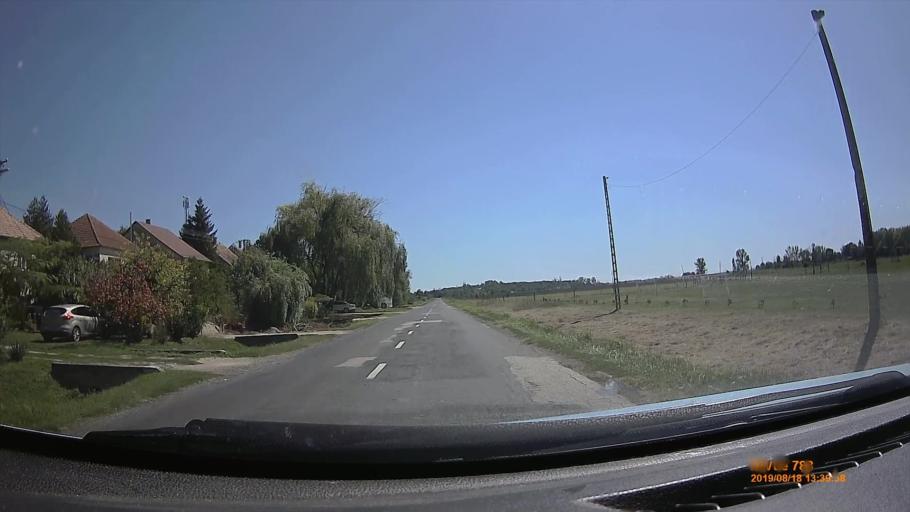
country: HU
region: Fejer
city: Cece
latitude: 46.7768
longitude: 18.5996
